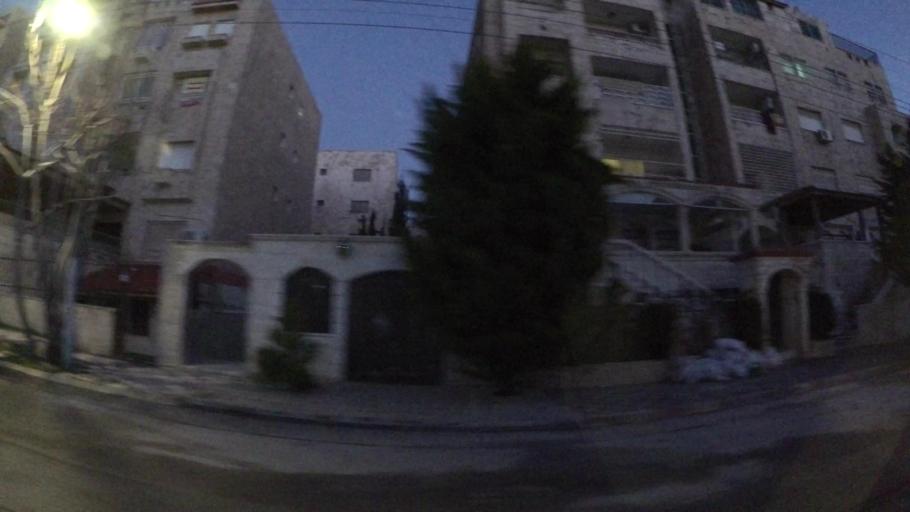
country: JO
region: Amman
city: Al Jubayhah
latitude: 31.9807
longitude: 35.8816
